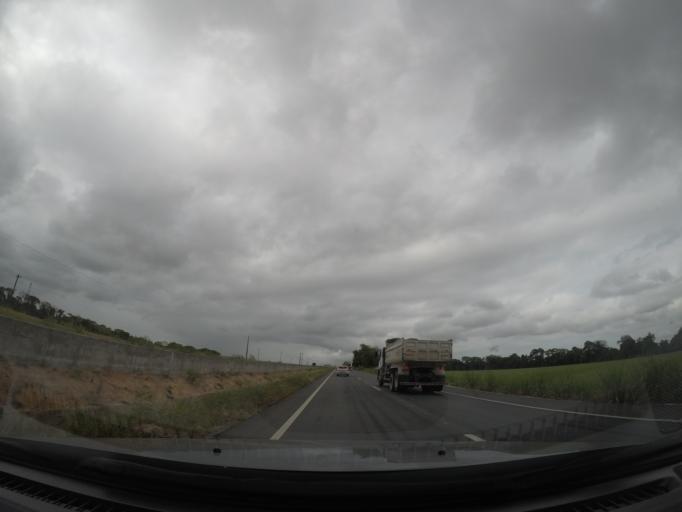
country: BR
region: Alagoas
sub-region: Pilar
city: Pilar
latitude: -9.6110
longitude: -36.0277
